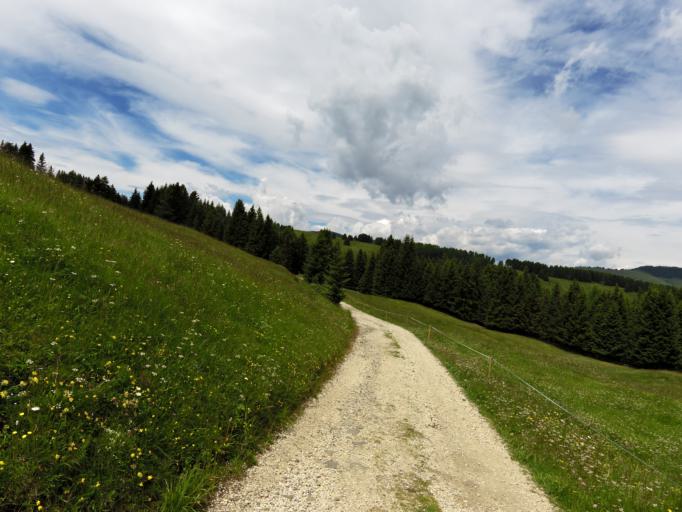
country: IT
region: Trentino-Alto Adige
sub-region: Bolzano
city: Ortisei
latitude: 46.5290
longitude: 11.6491
